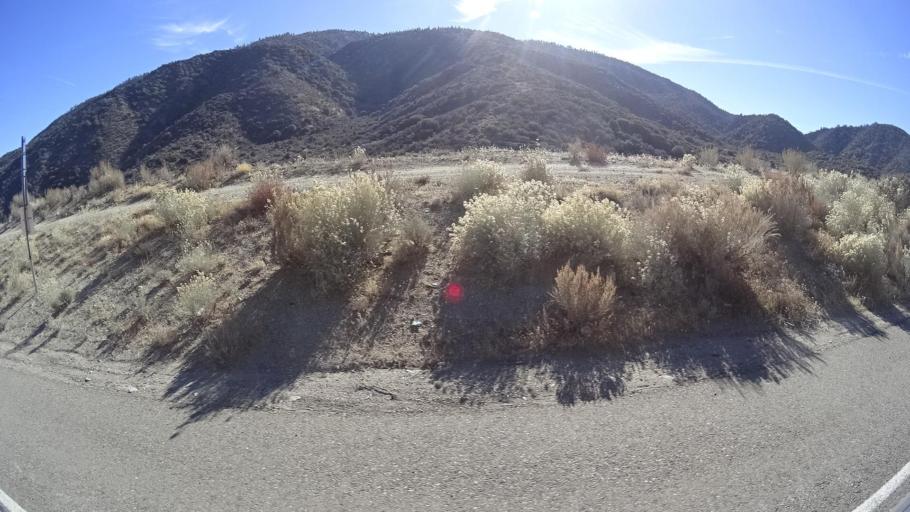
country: US
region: California
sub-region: Kern County
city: Frazier Park
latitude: 34.8221
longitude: -118.9696
